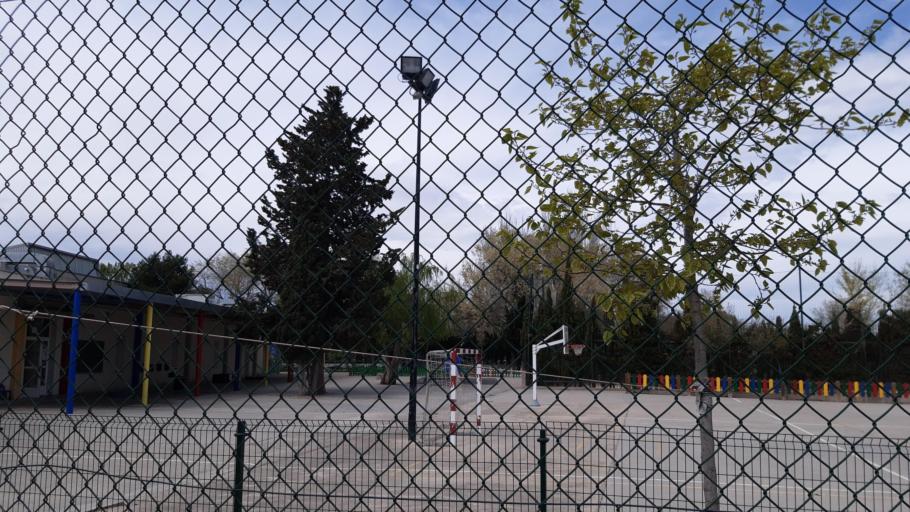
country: ES
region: Aragon
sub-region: Provincia de Zaragoza
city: Utebo
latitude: 41.7107
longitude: -0.9989
